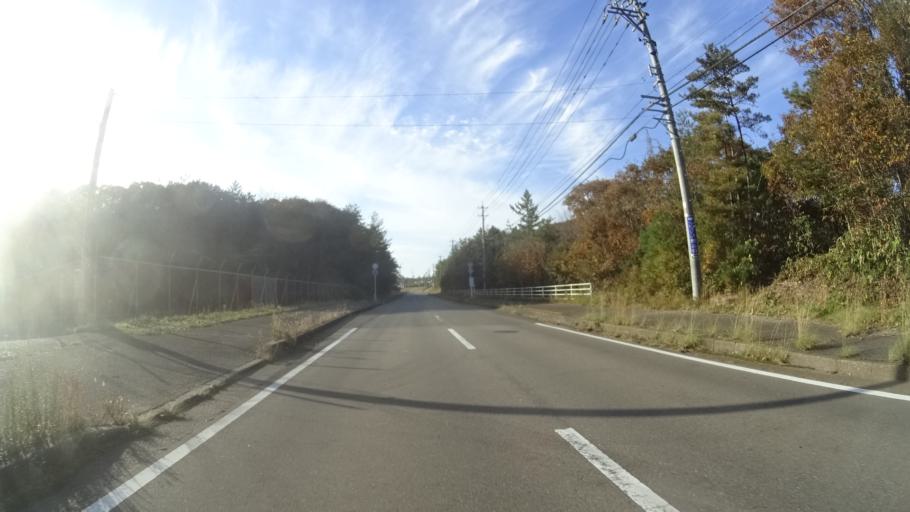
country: JP
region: Ishikawa
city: Hakui
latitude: 37.0675
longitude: 136.7600
